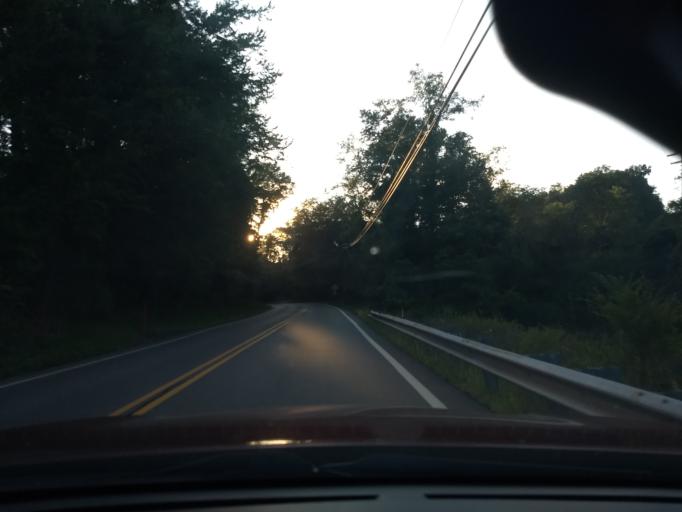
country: US
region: Pennsylvania
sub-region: Allegheny County
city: Bell Acres
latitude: 40.5963
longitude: -80.1324
